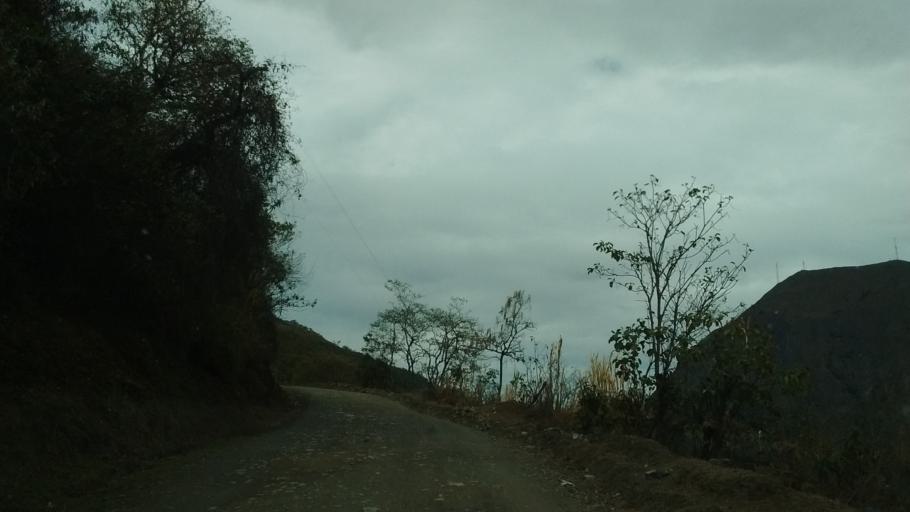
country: CO
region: Cauca
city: Almaguer
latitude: 1.8602
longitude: -76.9347
